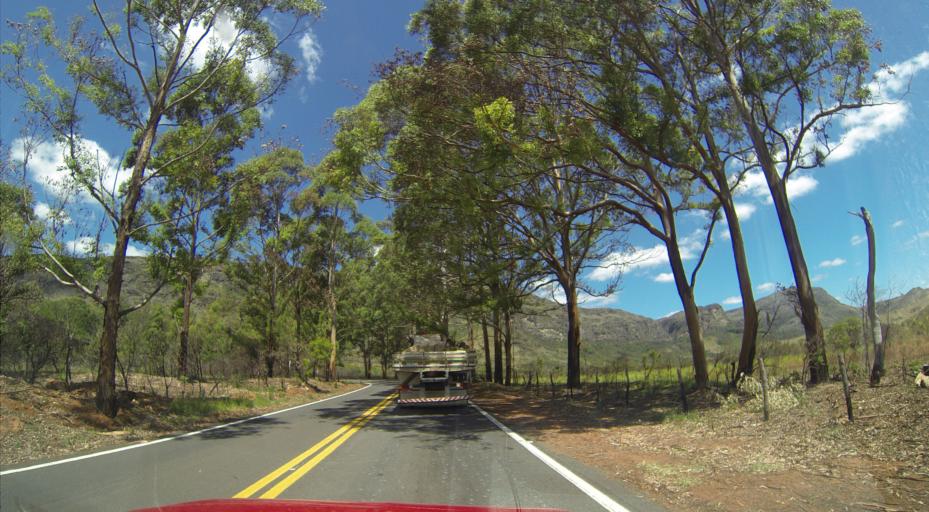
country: BR
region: Minas Gerais
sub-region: Conceicao Do Mato Dentro
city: Conceicao do Mato Dentro
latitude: -19.2814
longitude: -43.5510
